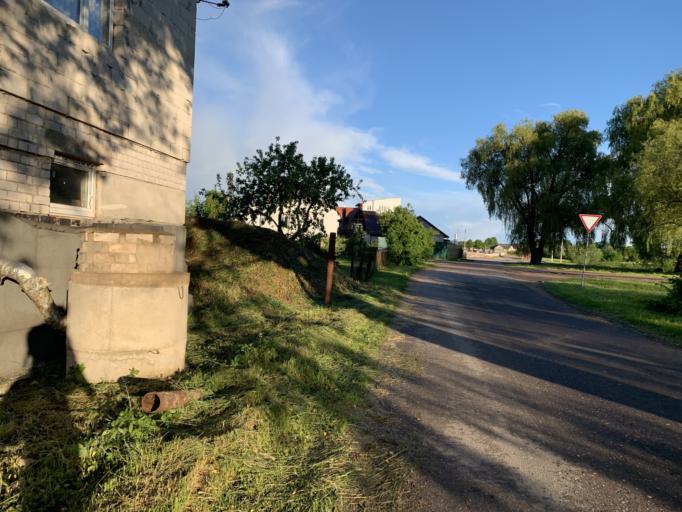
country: BY
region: Minsk
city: Nyasvizh
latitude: 53.2114
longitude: 26.6928
